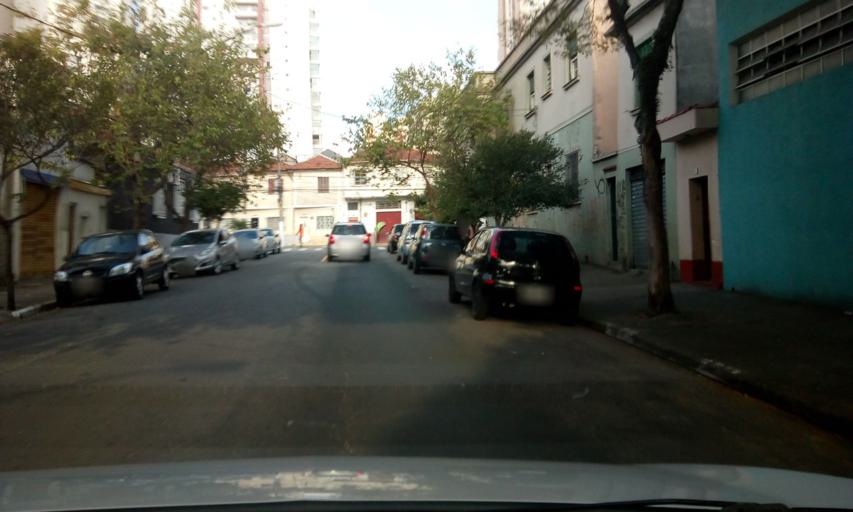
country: BR
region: Sao Paulo
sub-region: Sao Paulo
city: Sao Paulo
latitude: -23.5483
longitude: -46.5928
